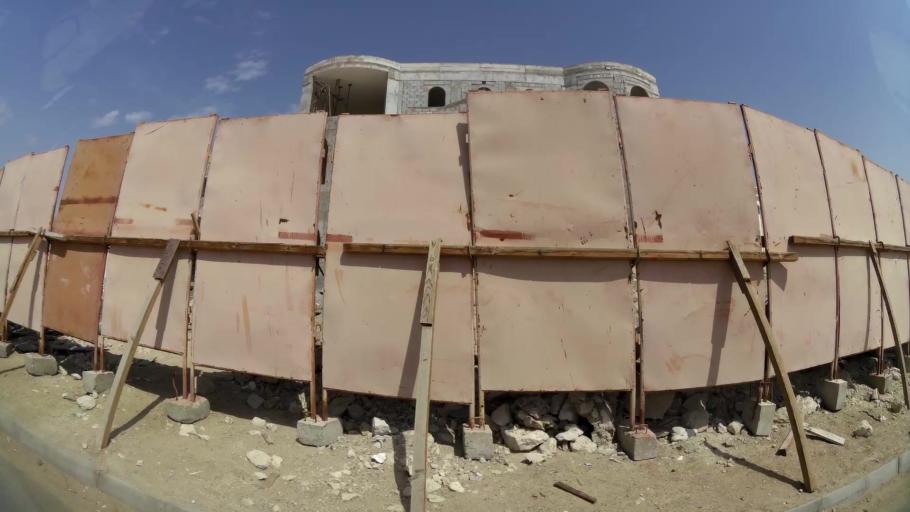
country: AE
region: Abu Dhabi
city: Abu Dhabi
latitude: 24.2937
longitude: 54.6509
